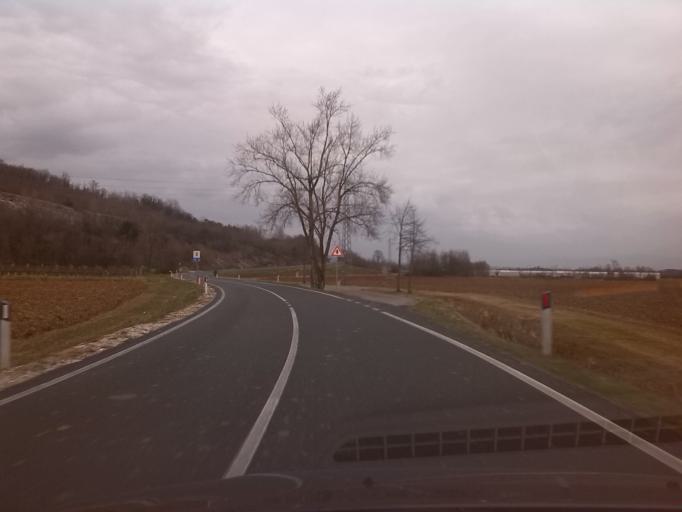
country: IT
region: Friuli Venezia Giulia
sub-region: Provincia di Gorizia
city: Medea
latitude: 45.9199
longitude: 13.4371
